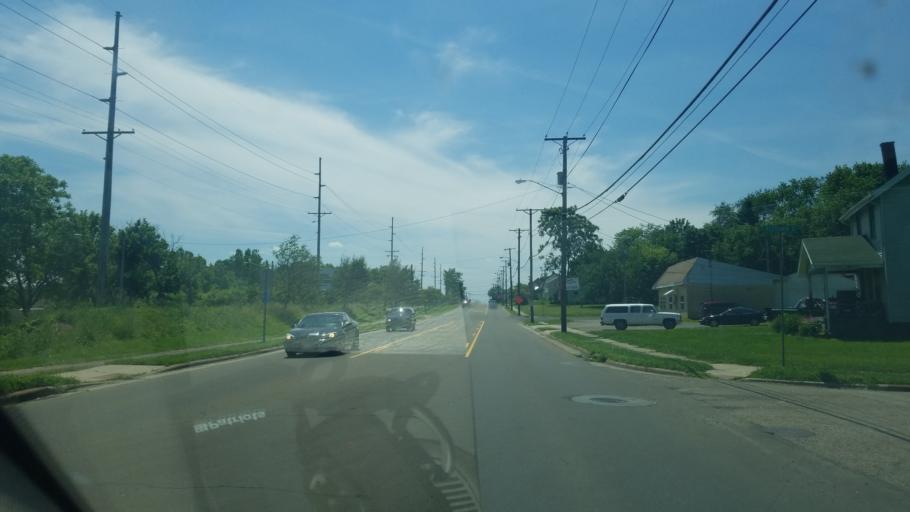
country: US
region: Ohio
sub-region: Stark County
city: East Canton
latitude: 40.8210
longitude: -81.3219
